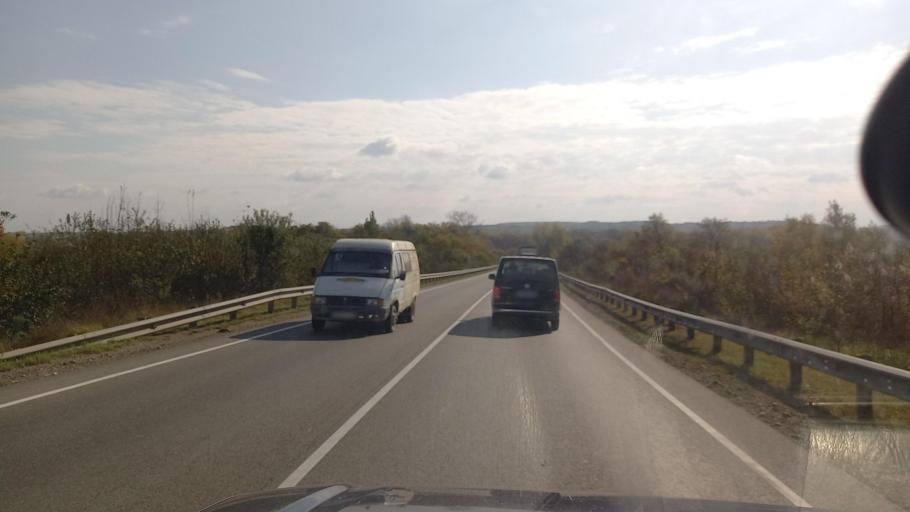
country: RU
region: Krasnodarskiy
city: Abinsk
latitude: 44.8469
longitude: 38.1485
